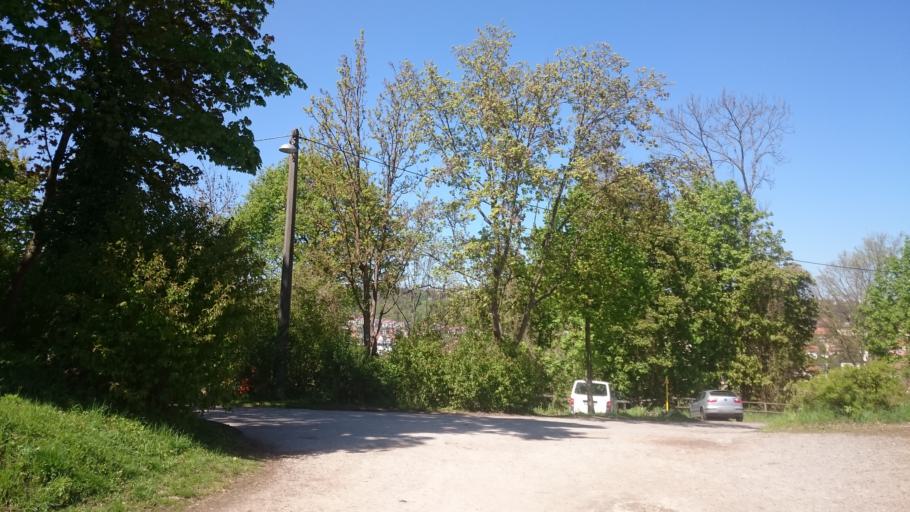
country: DE
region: Baden-Wuerttemberg
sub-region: Tuebingen Region
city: Tuebingen
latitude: 48.5193
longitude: 9.0489
